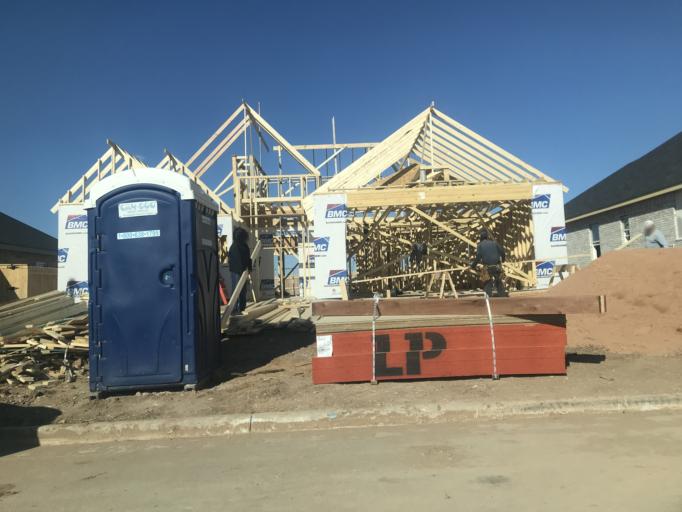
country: US
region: Texas
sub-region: Taylor County
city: Potosi
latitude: 32.3686
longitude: -99.7229
